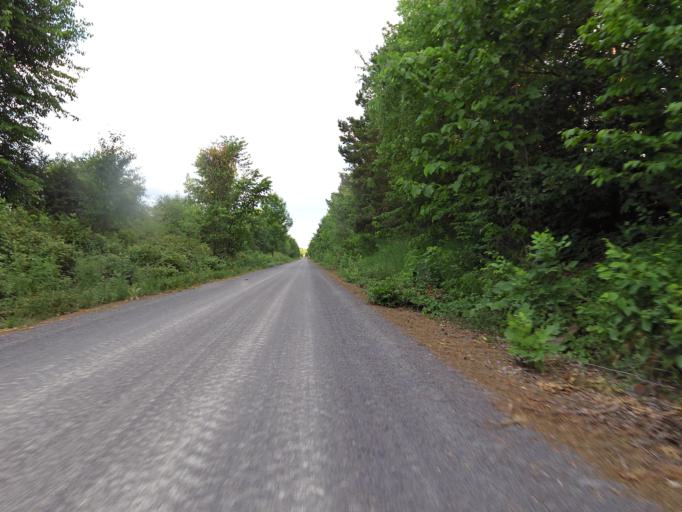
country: CA
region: Ontario
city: Arnprior
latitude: 45.3373
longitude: -76.2963
